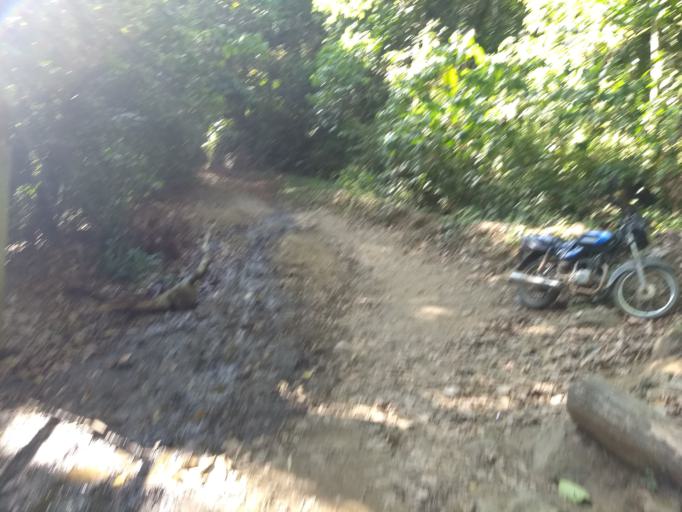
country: CO
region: Magdalena
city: Santa Marta
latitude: 11.1462
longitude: -74.1095
